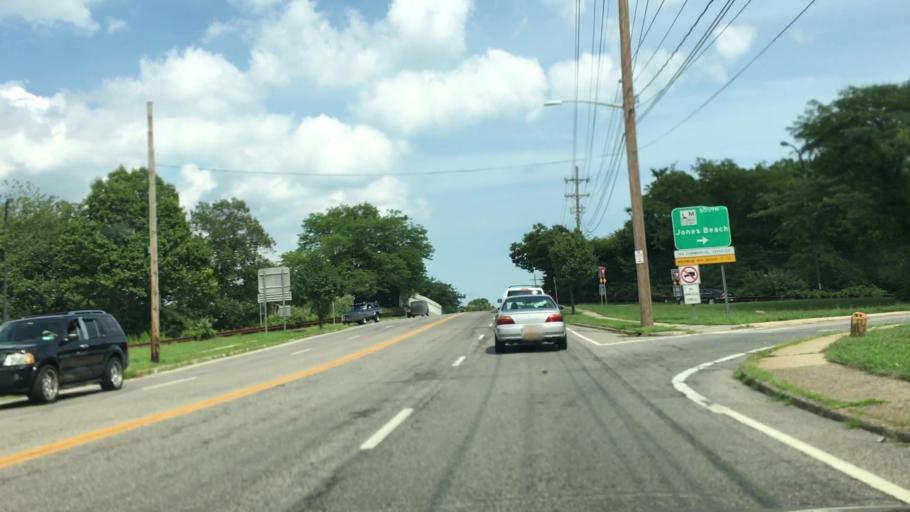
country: US
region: New York
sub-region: Nassau County
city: Freeport
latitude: 40.6653
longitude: -73.5702
